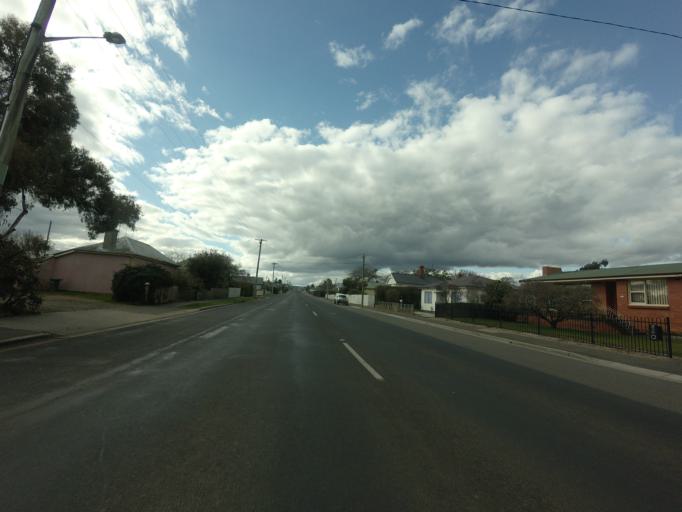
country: AU
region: Tasmania
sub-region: Northern Midlands
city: Longford
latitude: -41.6009
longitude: 147.1200
